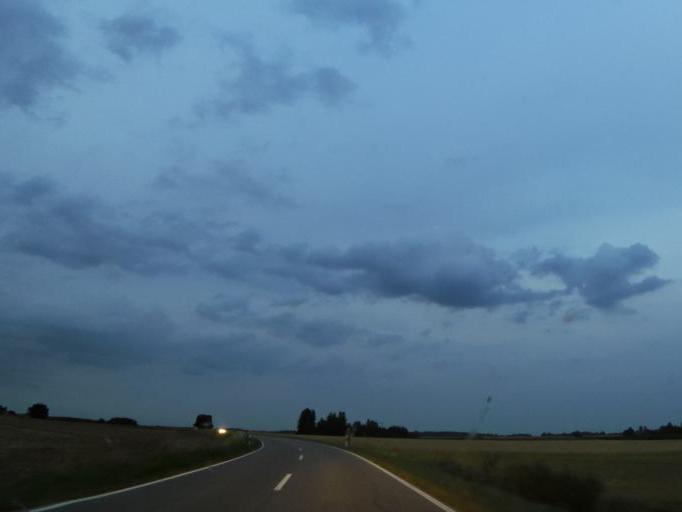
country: DE
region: Bavaria
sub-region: Upper Bavaria
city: Buch am Buchrain
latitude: 48.2100
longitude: 11.9687
